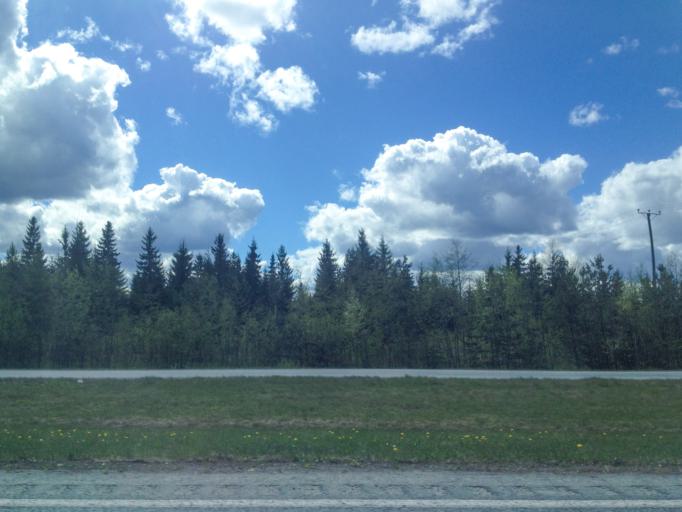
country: FI
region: Haeme
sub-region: Haemeenlinna
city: Kalvola
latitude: 61.0884
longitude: 24.1936
